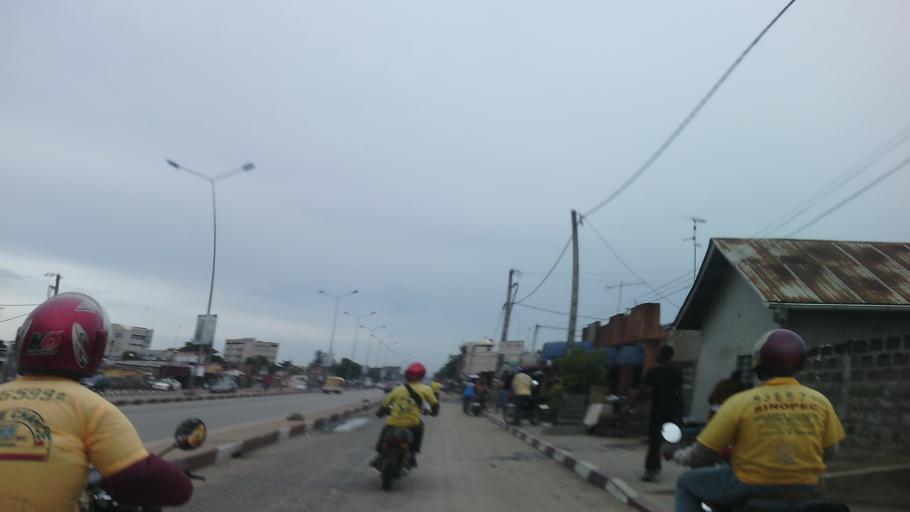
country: BJ
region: Littoral
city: Cotonou
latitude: 6.3694
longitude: 2.4113
